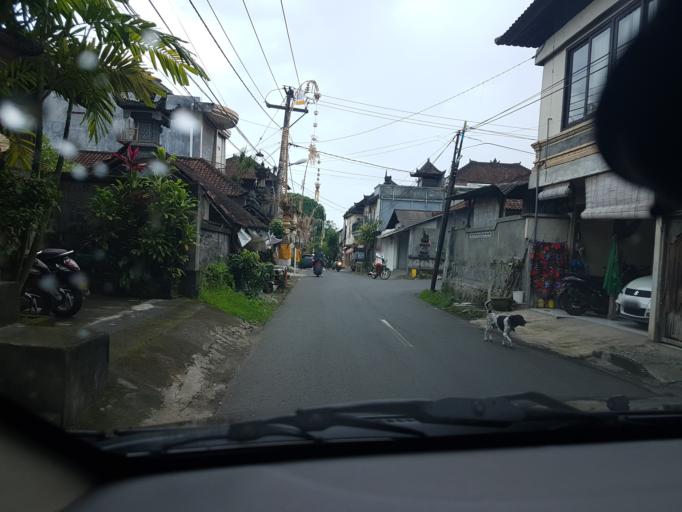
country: ID
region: Bali
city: Banjar Pande
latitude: -8.5077
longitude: 115.2484
